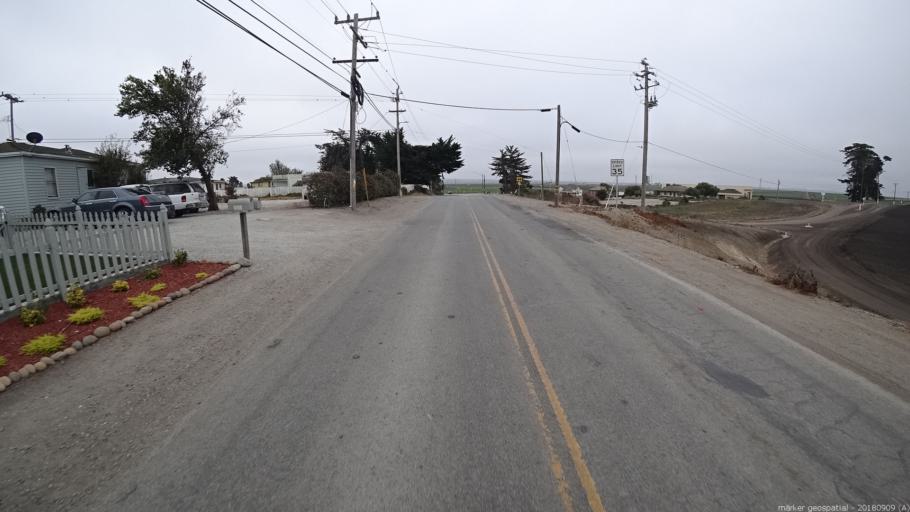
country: US
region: California
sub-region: Monterey County
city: Boronda
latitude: 36.7012
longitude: -121.6765
